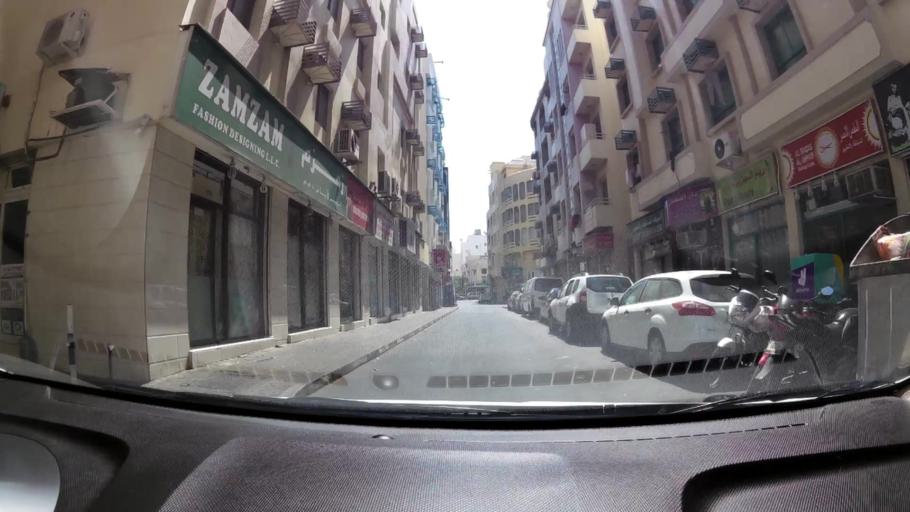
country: AE
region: Ash Shariqah
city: Sharjah
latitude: 25.2771
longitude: 55.3118
